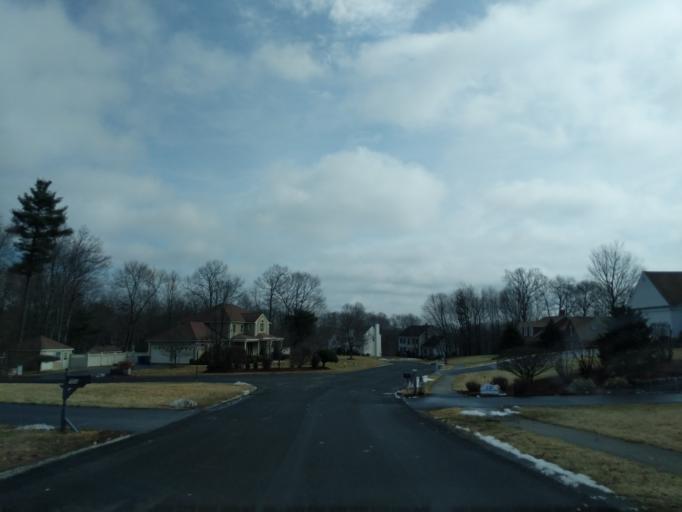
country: US
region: Massachusetts
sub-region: Worcester County
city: Whitinsville
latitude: 42.1039
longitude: -71.6760
